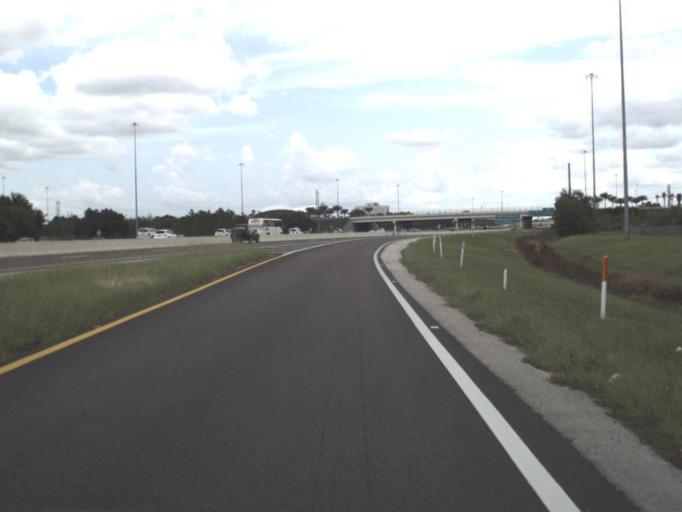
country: US
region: Florida
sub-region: Hillsborough County
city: East Lake-Orient Park
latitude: 27.9961
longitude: -82.3524
